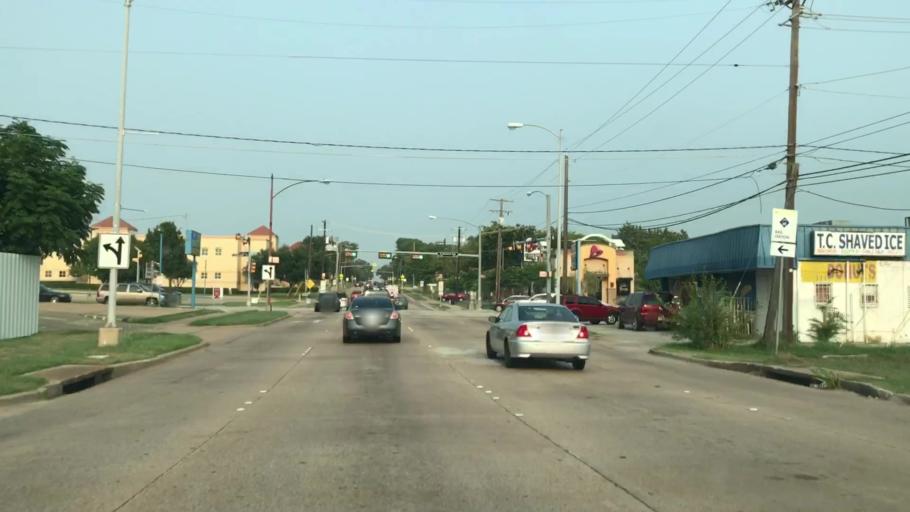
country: US
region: Texas
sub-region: Dallas County
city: Garland
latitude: 32.9090
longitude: -96.6489
